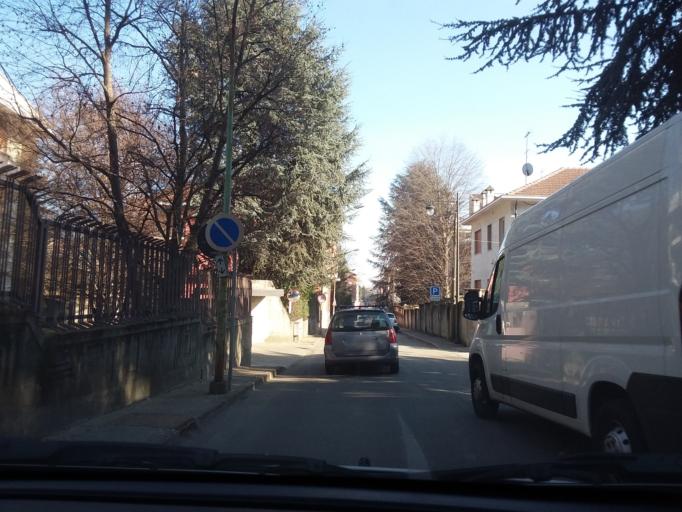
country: IT
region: Piedmont
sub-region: Provincia di Torino
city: Rivoli
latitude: 45.0747
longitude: 7.5180
